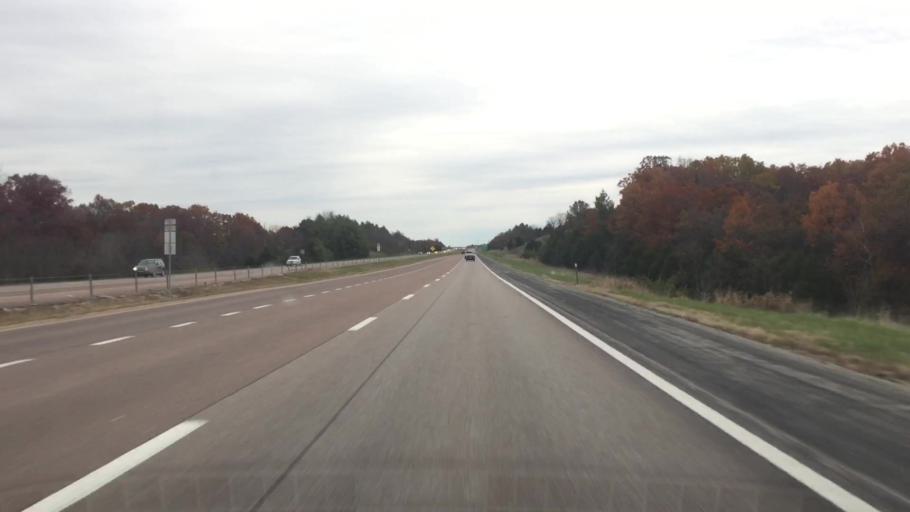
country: US
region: Missouri
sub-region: Boone County
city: Ashland
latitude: 38.7508
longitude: -92.2531
